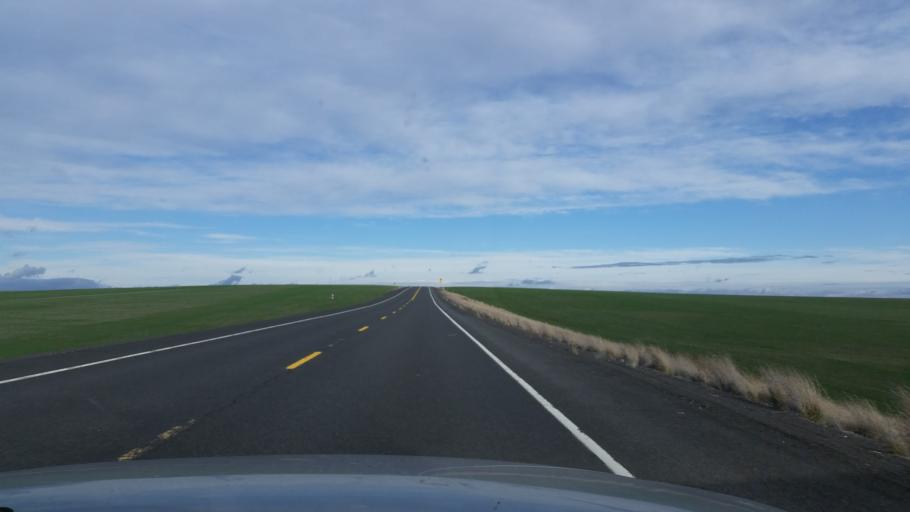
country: US
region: Washington
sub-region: Adams County
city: Ritzville
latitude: 47.4035
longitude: -118.3876
